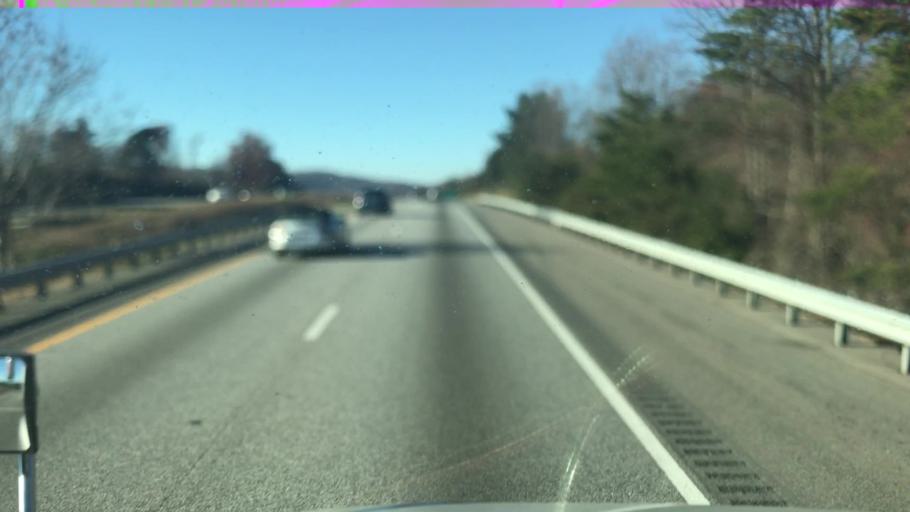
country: US
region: Virginia
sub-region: City of Salem
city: Salem
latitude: 37.2610
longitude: -80.1674
